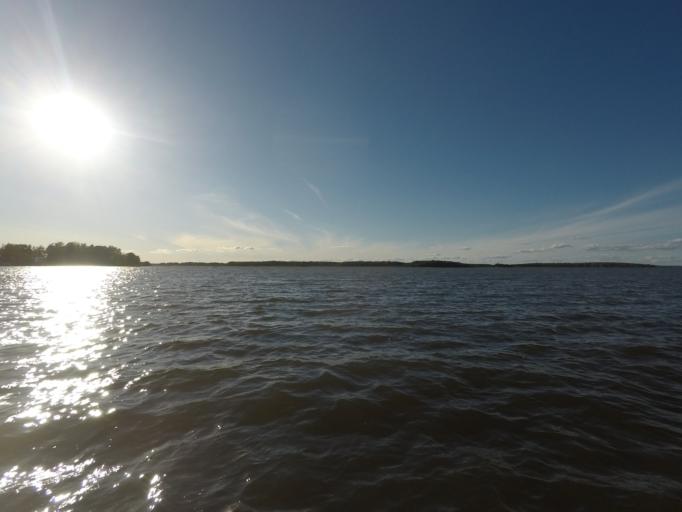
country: SE
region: Vaestmanland
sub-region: Vasteras
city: Vasteras
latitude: 59.5177
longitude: 16.5701
